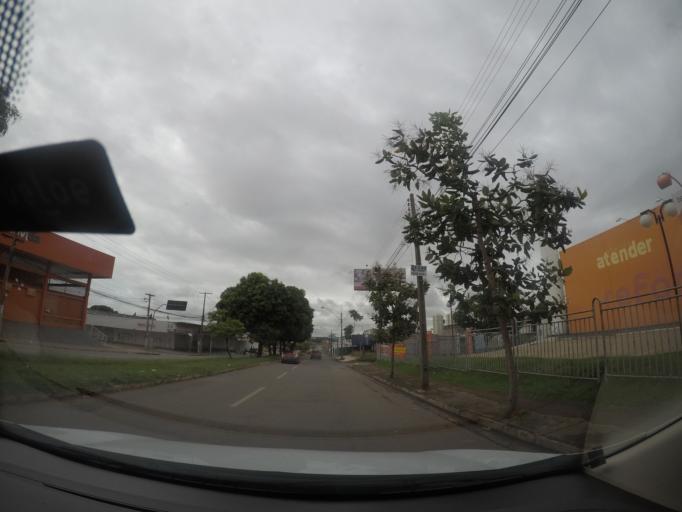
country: BR
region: Goias
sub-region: Goiania
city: Goiania
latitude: -16.7452
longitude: -49.2825
